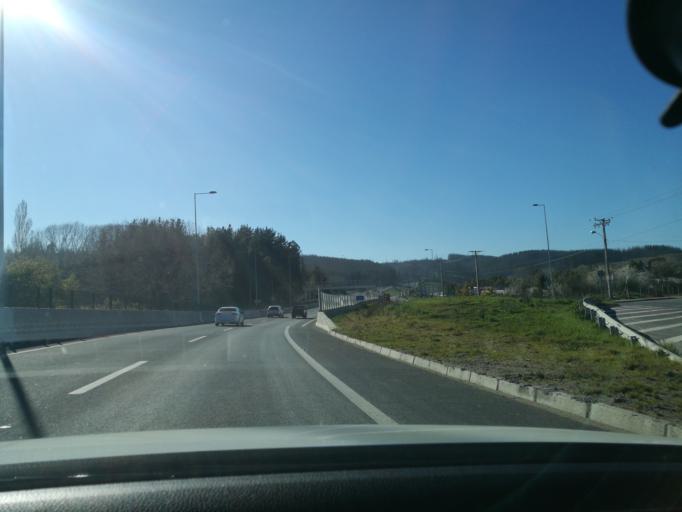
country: CL
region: Biobio
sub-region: Provincia de Concepcion
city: Penco
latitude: -36.8562
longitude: -72.8788
